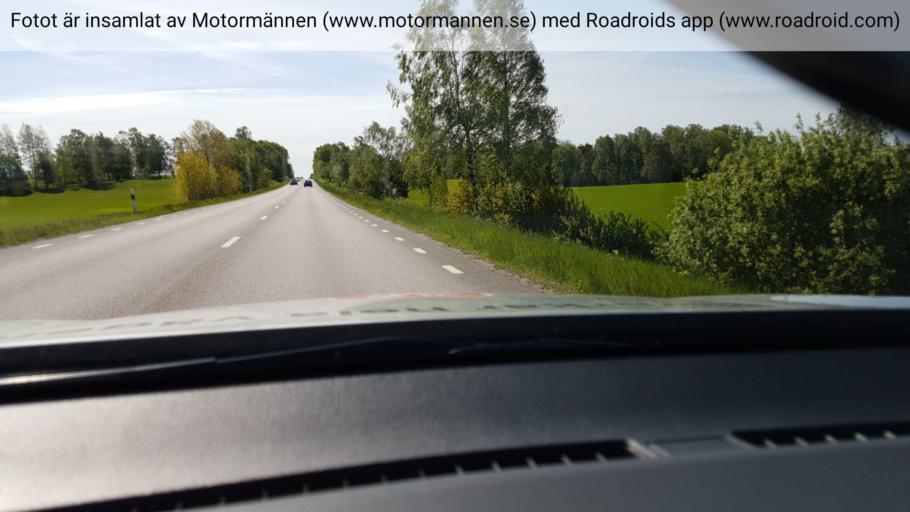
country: SE
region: Vaestra Goetaland
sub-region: Hjo Kommun
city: Hjo
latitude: 58.3315
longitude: 14.2542
